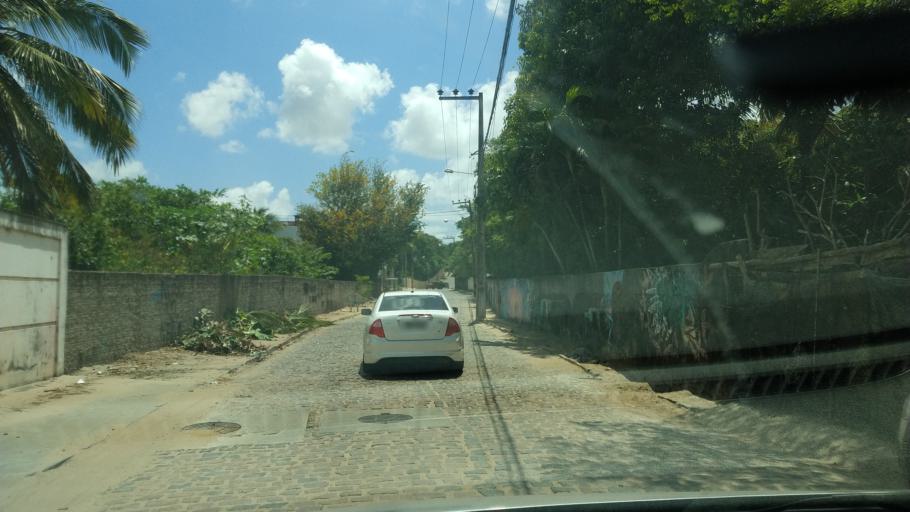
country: BR
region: Rio Grande do Norte
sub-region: Ares
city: Ares
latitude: -6.2323
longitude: -35.0535
